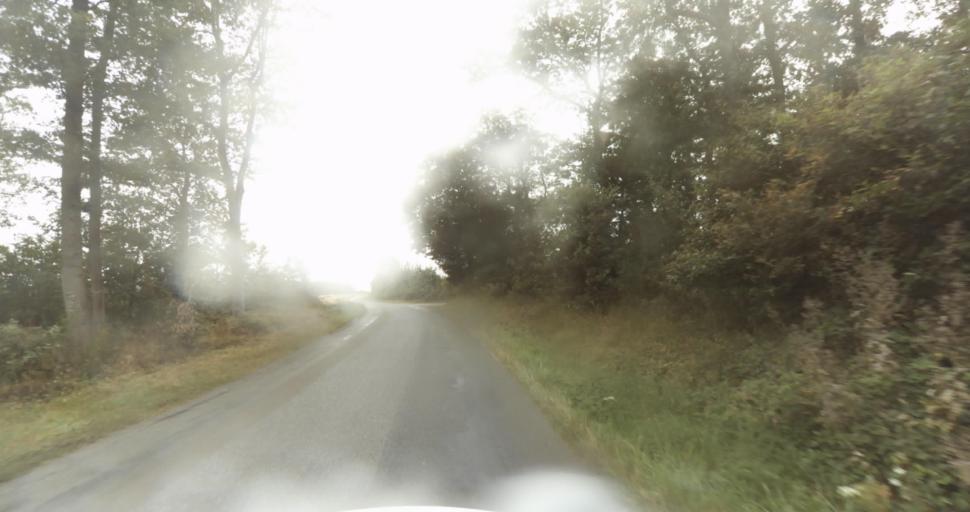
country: FR
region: Centre
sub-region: Departement d'Eure-et-Loir
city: Saint-Lubin-des-Joncherets
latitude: 48.7750
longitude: 1.2300
